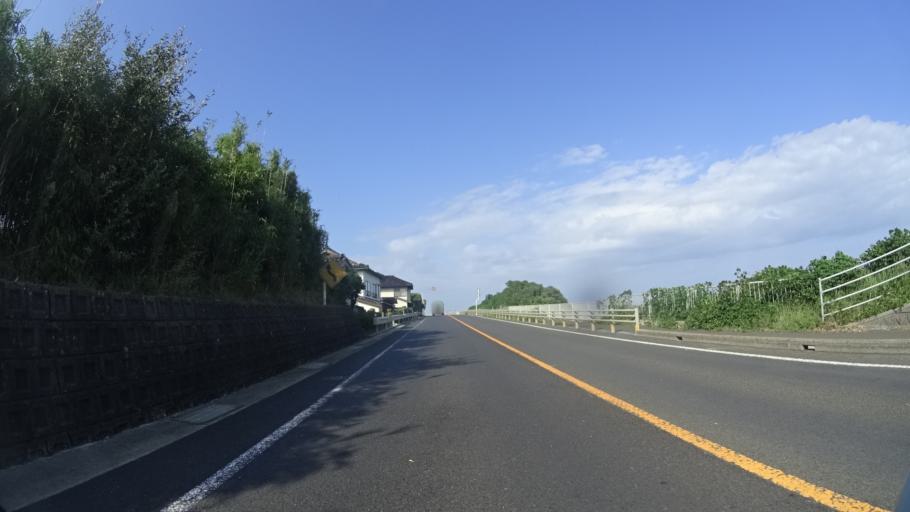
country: JP
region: Shimane
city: Odacho-oda
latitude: 35.2831
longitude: 132.6207
